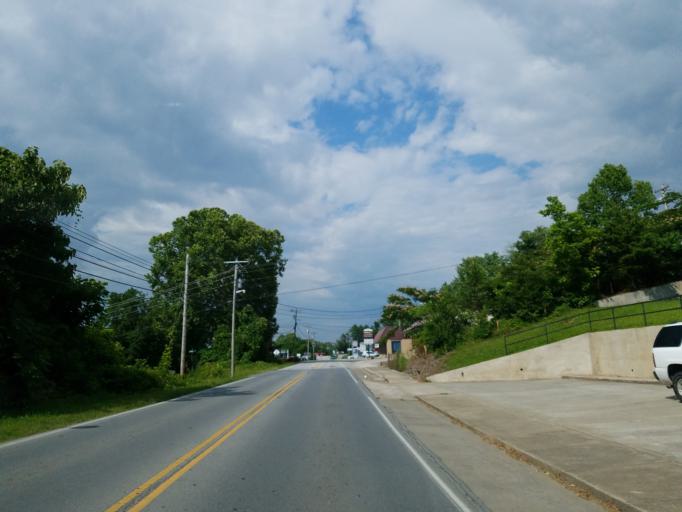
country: US
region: Georgia
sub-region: Fannin County
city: Blue Ridge
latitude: 34.8683
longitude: -84.3206
